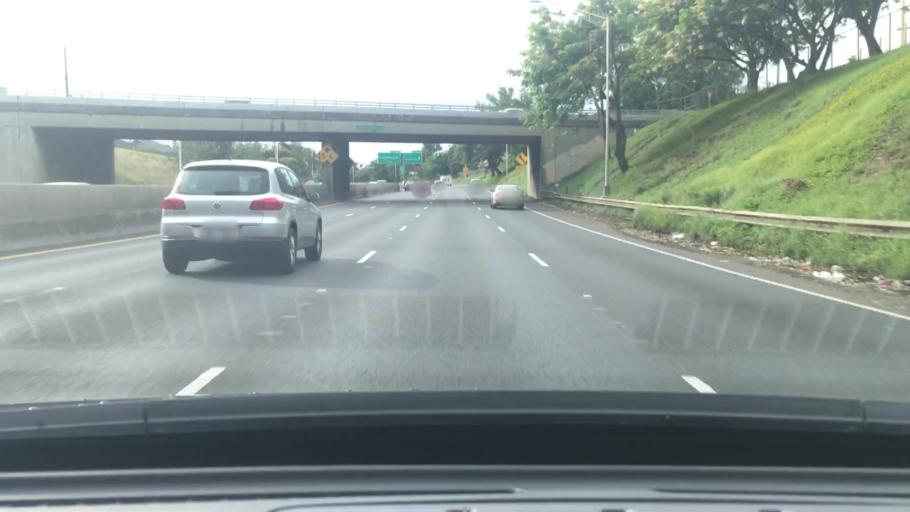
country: US
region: Hawaii
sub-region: Honolulu County
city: Honolulu
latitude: 21.3217
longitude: -157.8603
